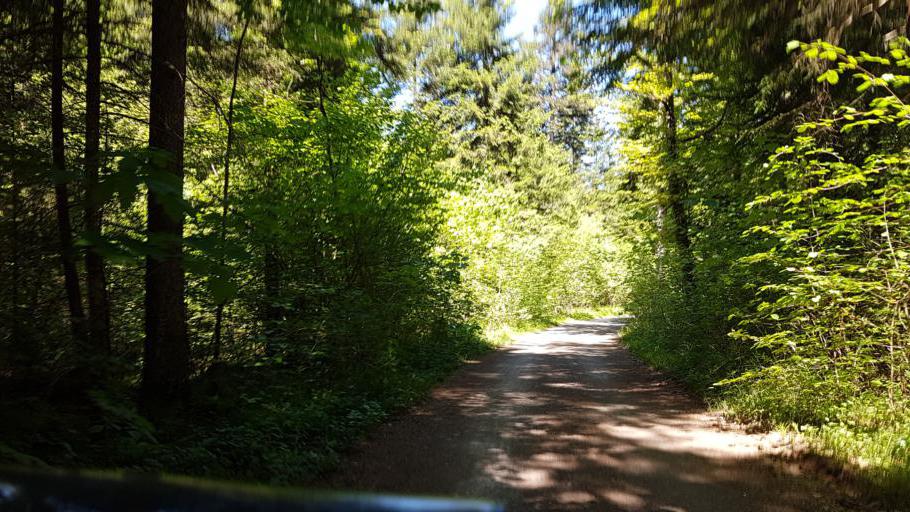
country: CH
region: Bern
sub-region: Thun District
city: Thun
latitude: 46.7207
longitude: 7.6063
